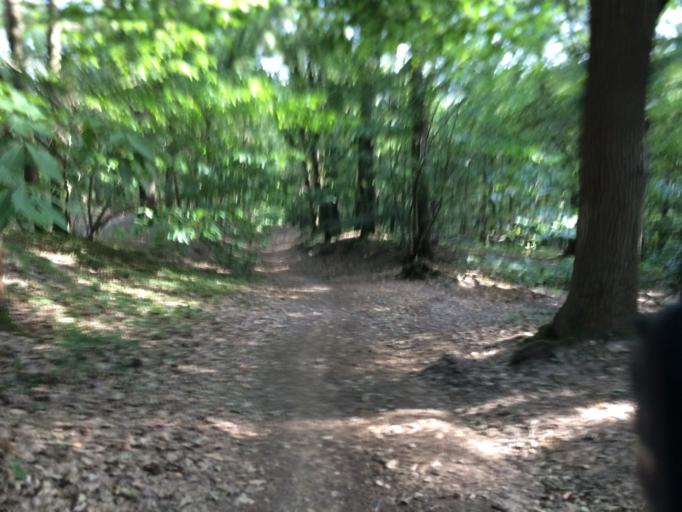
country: FR
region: Ile-de-France
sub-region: Departement de l'Essonne
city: Igny
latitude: 48.7440
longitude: 2.2378
